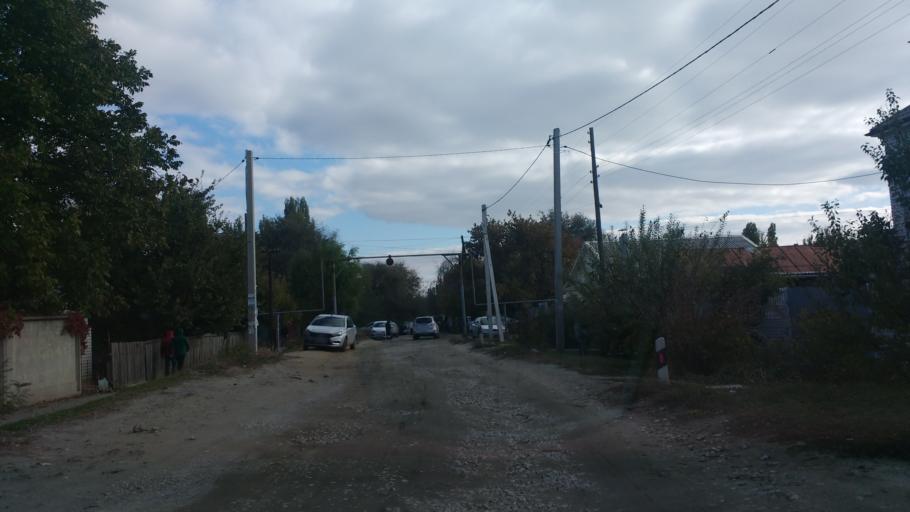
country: RU
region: Volgograd
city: Volgograd
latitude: 48.7553
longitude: 44.5456
